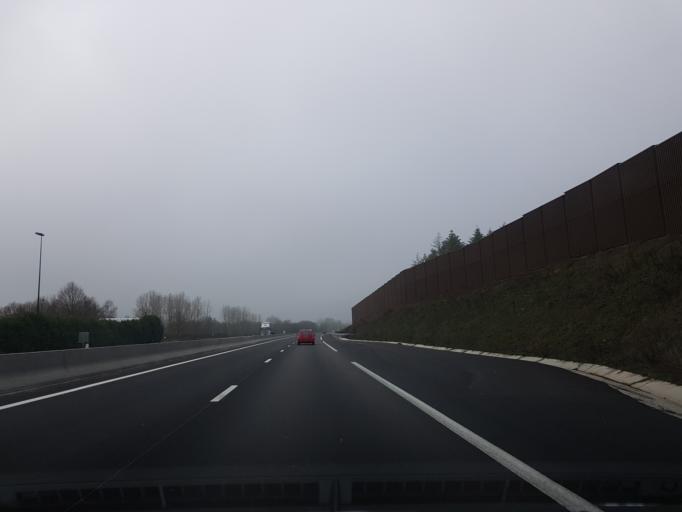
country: FR
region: Bourgogne
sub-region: Departement de Saone-et-Loire
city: Montchanin
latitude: 46.7325
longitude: 4.4713
